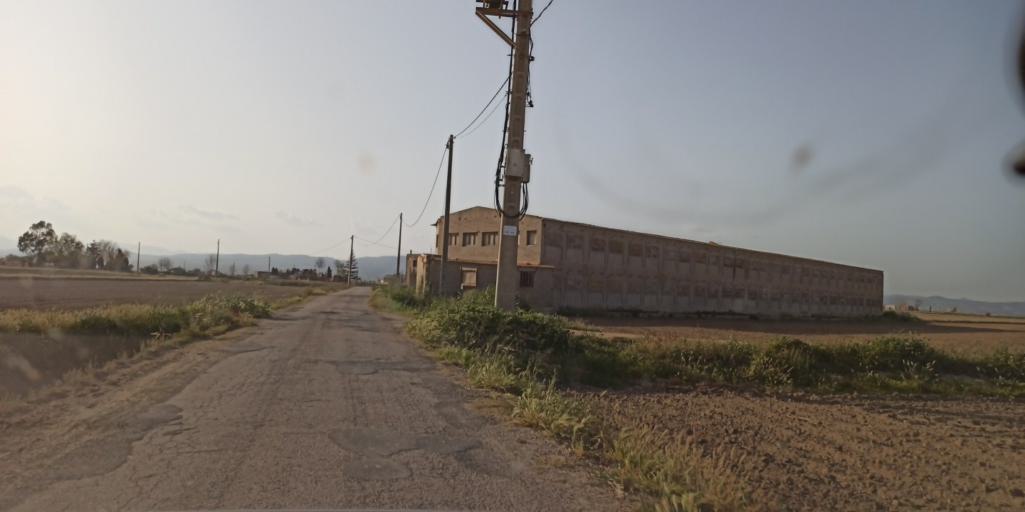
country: ES
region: Catalonia
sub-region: Provincia de Tarragona
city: Deltebre
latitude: 40.7534
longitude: 0.7564
